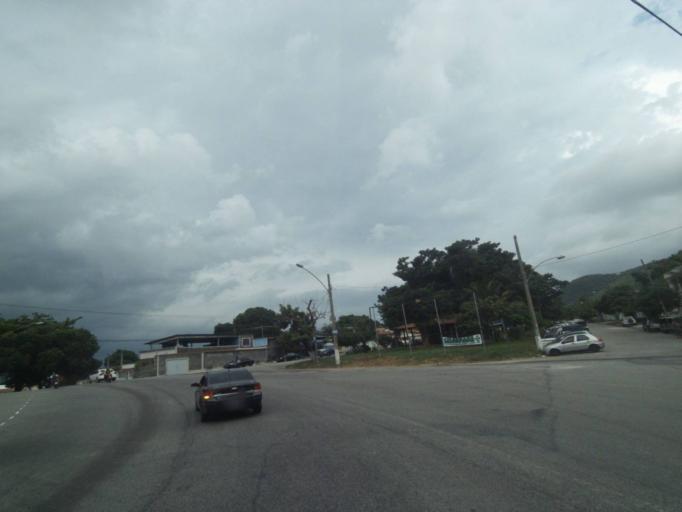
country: BR
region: Rio de Janeiro
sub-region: Nilopolis
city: Nilopolis
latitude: -22.8909
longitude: -43.3911
